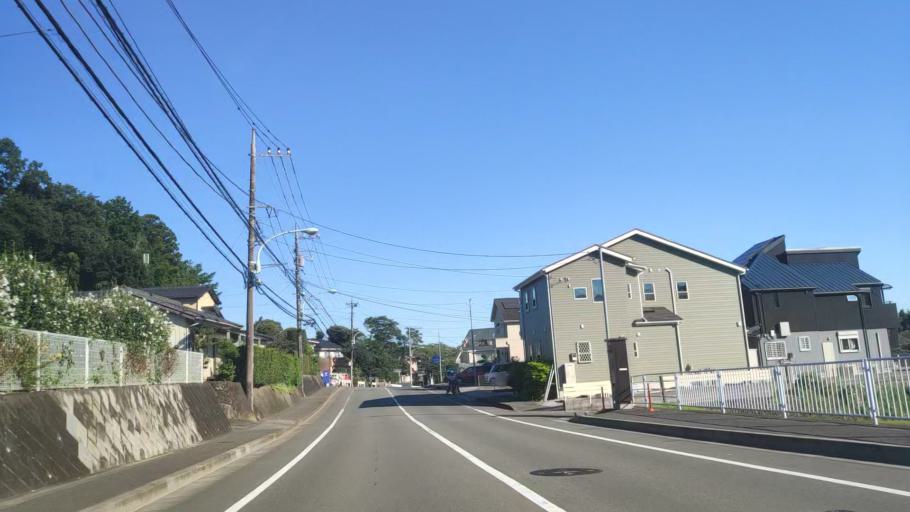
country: JP
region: Tokyo
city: Hachioji
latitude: 35.6072
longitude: 139.3148
